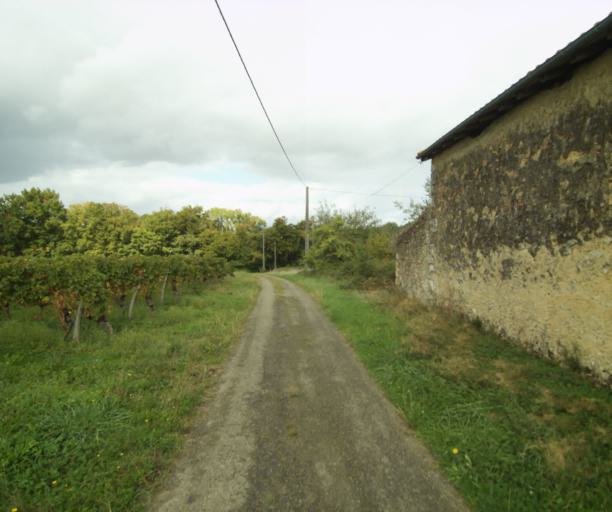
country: FR
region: Midi-Pyrenees
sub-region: Departement du Gers
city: Eauze
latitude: 43.8512
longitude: 0.0523
